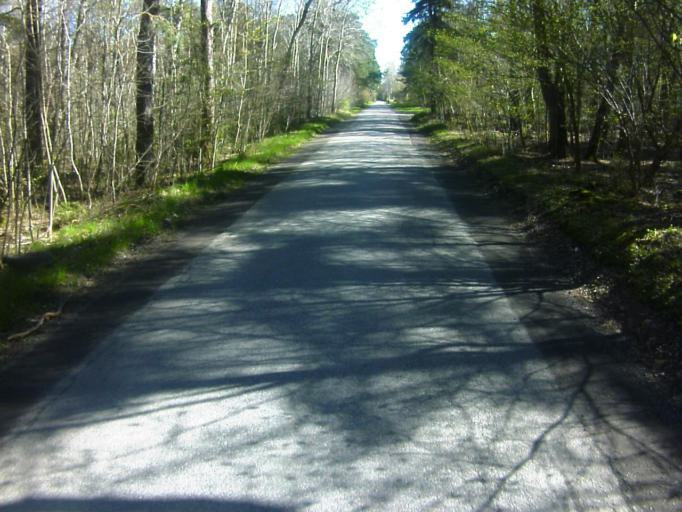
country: SE
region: Skane
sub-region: Kavlinge Kommun
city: Hofterup
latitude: 55.8118
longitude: 12.9868
